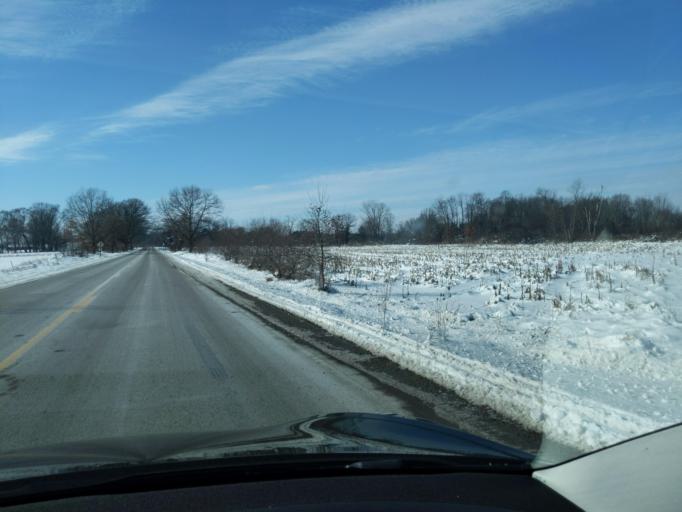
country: US
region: Michigan
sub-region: Ingham County
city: Stockbridge
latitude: 42.5037
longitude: -84.0741
